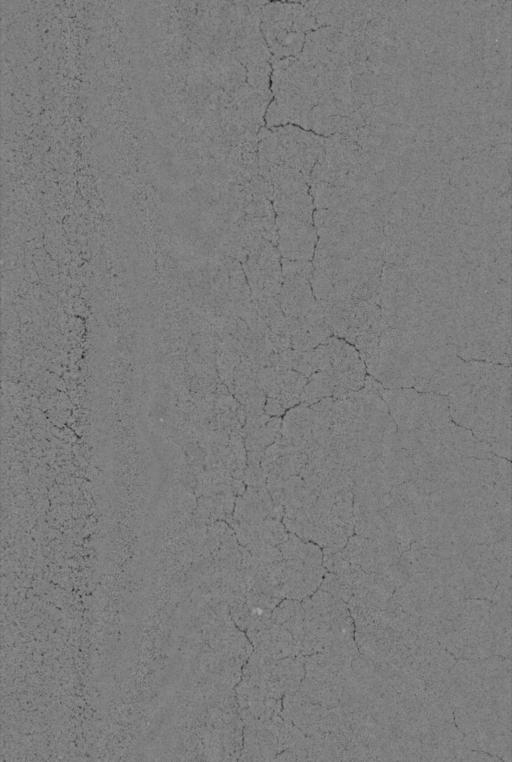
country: US
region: Maryland
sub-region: Prince George's County
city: Coral Hills
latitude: 38.8723
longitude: -76.9471
